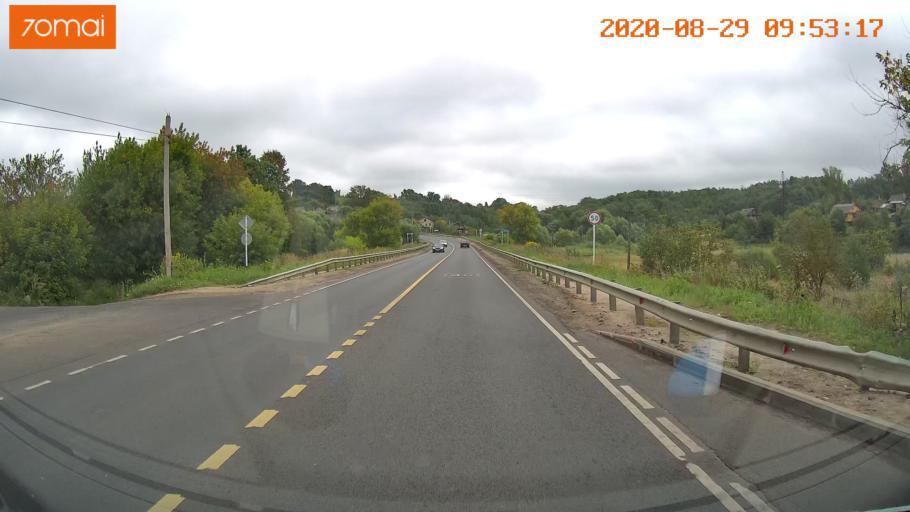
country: RU
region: Ivanovo
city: Zarechnyy
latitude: 57.4232
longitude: 42.2215
